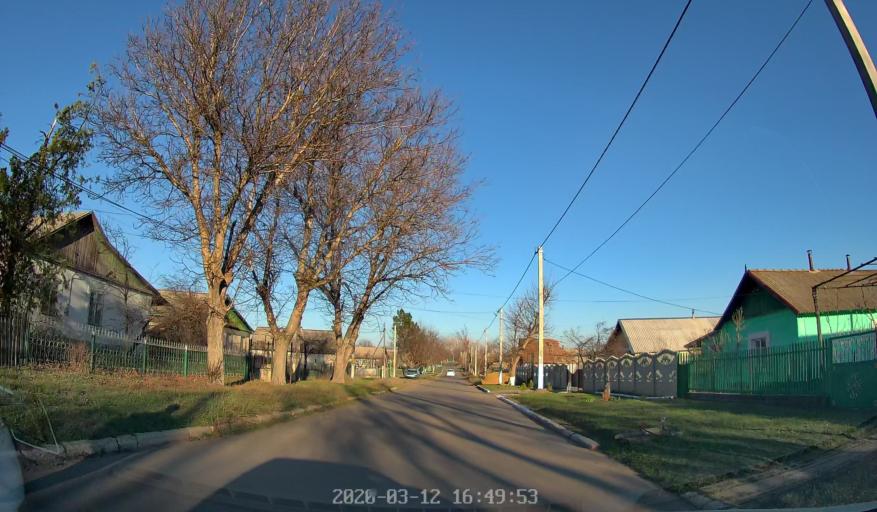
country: MD
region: Anenii Noi
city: Anenii Noi
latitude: 46.8138
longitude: 29.2061
